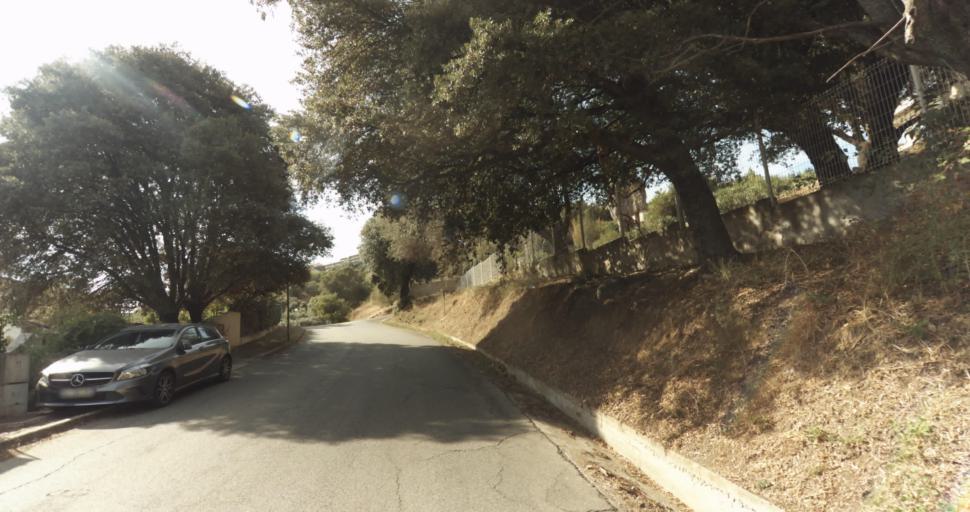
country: FR
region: Corsica
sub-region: Departement de la Corse-du-Sud
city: Ajaccio
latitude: 41.9338
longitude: 8.7222
